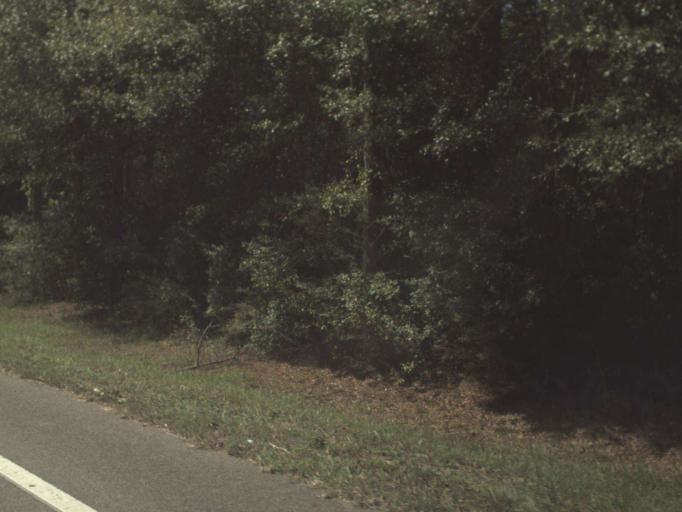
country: US
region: Florida
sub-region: Walton County
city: Freeport
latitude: 30.4762
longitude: -85.9626
